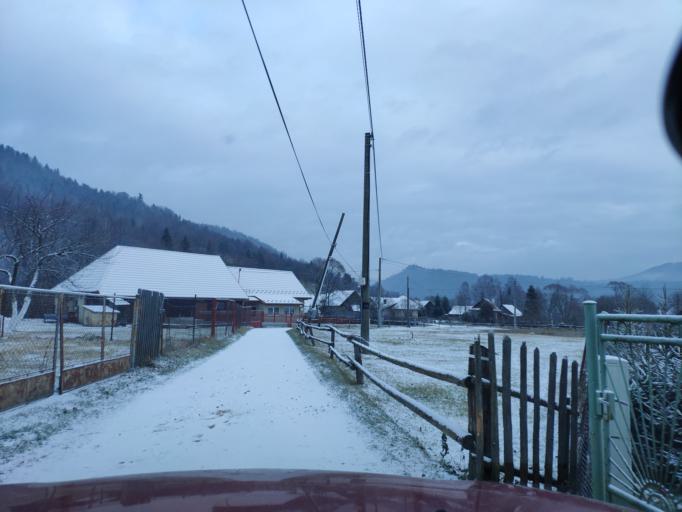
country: SK
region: Kosicky
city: Spisska Nova Ves
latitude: 48.8185
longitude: 20.5775
